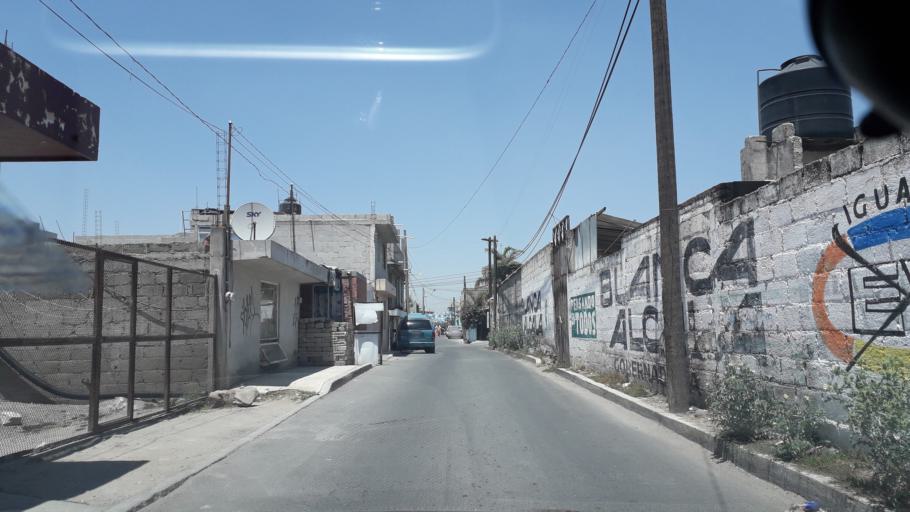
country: MX
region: Puebla
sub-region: Puebla
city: Santa Maria Xonacatepec
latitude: 19.0879
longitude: -98.1009
